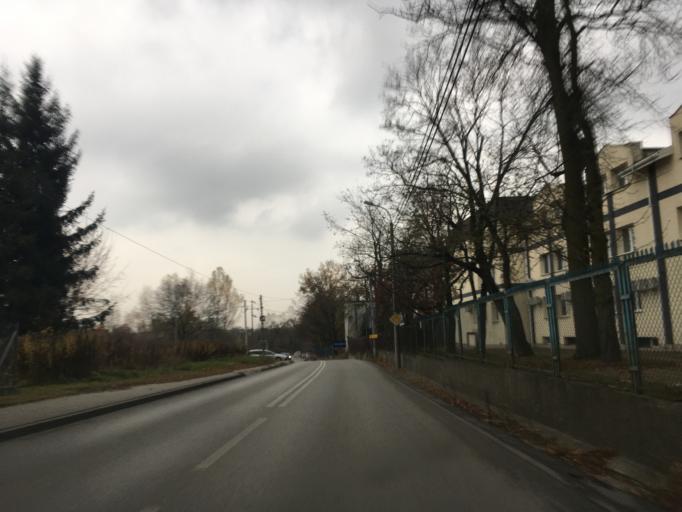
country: PL
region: Masovian Voivodeship
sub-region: Powiat piaseczynski
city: Piaseczno
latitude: 52.0491
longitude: 21.0059
